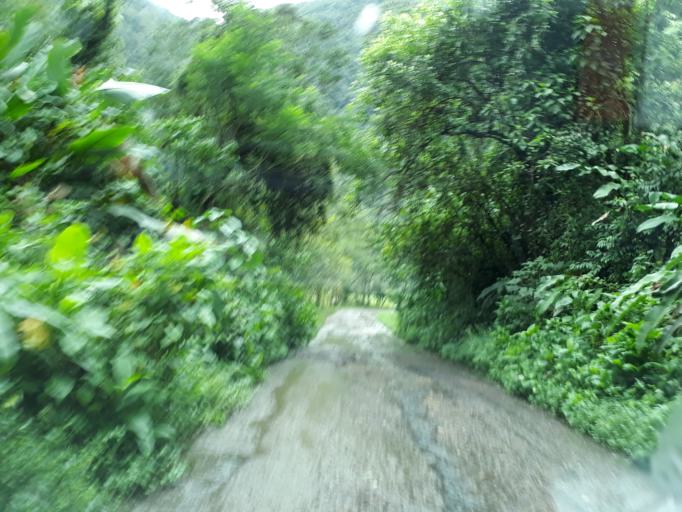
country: CO
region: Boyaca
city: Santa Maria
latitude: 4.7476
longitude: -73.3082
